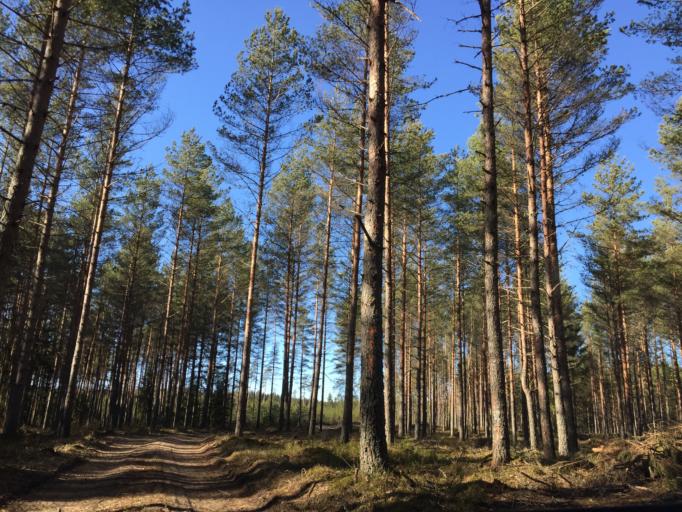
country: LV
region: Ropazu
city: Ropazi
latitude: 56.8890
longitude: 24.7105
